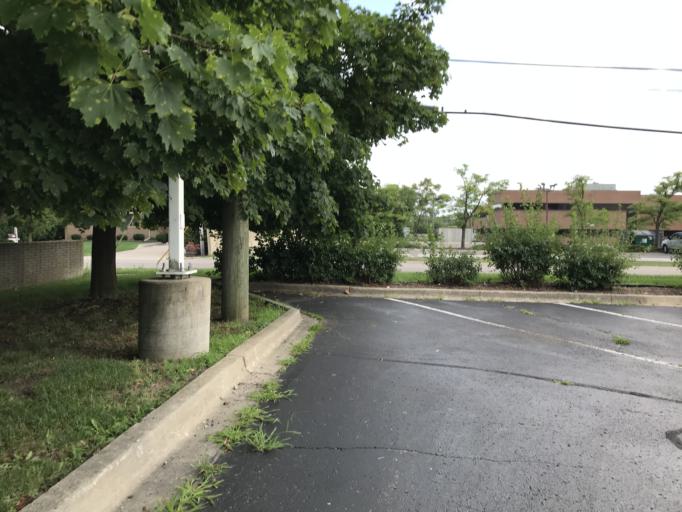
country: US
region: Michigan
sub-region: Oakland County
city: Farmington
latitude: 42.4686
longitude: -83.3557
